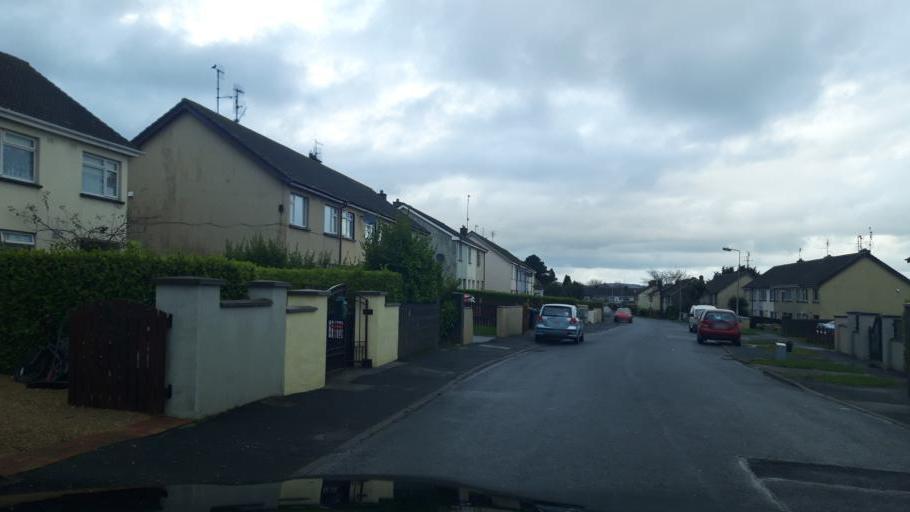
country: IE
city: Newtownmountkennedy
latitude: 53.0854
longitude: -6.1124
